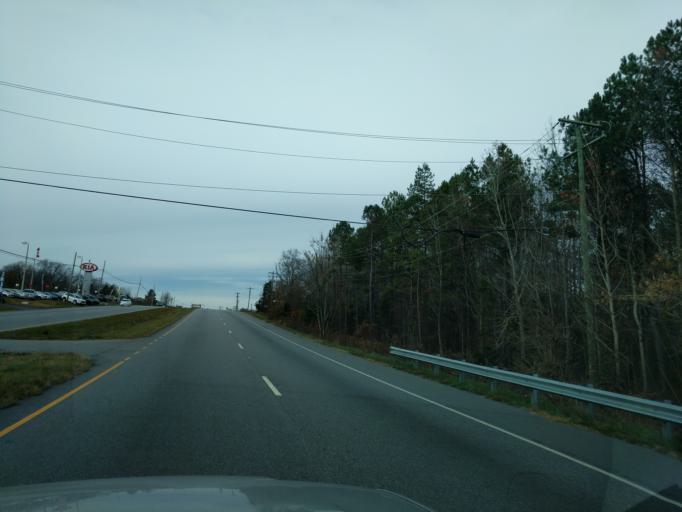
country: US
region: South Carolina
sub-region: Anderson County
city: Northlake
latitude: 34.5824
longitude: -82.7338
